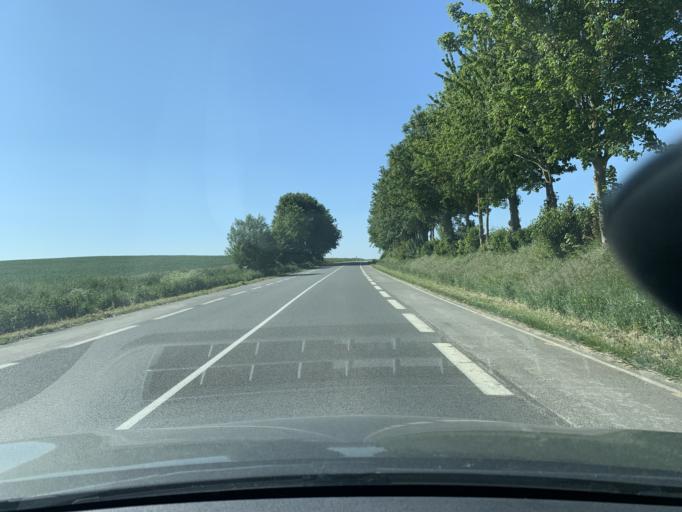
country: FR
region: Nord-Pas-de-Calais
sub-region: Departement du Nord
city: Rumilly-en-Cambresis
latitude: 50.1260
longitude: 3.2462
